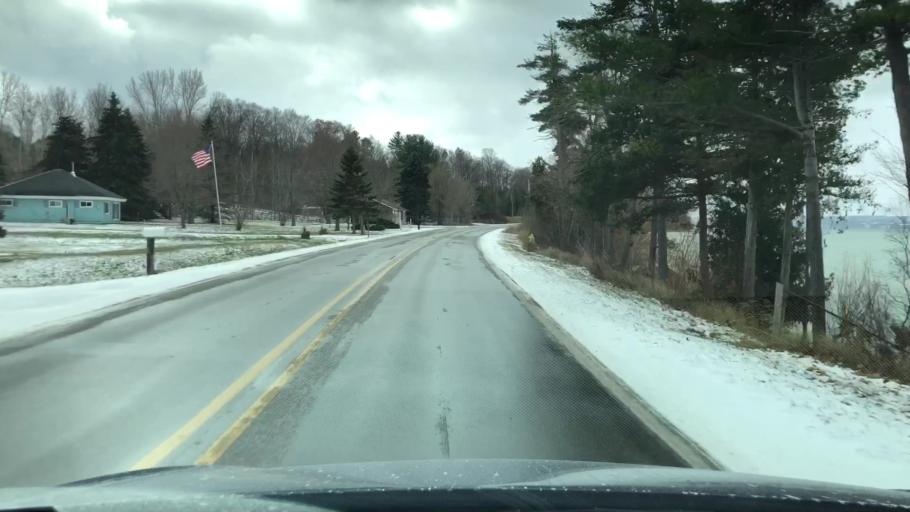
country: US
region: Michigan
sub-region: Leelanau County
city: Greilickville
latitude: 44.8434
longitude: -85.5580
